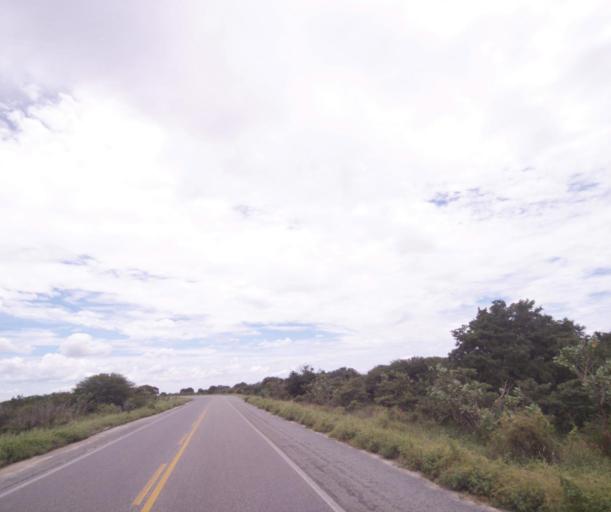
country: BR
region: Bahia
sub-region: Carinhanha
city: Carinhanha
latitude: -14.3130
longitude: -43.7851
